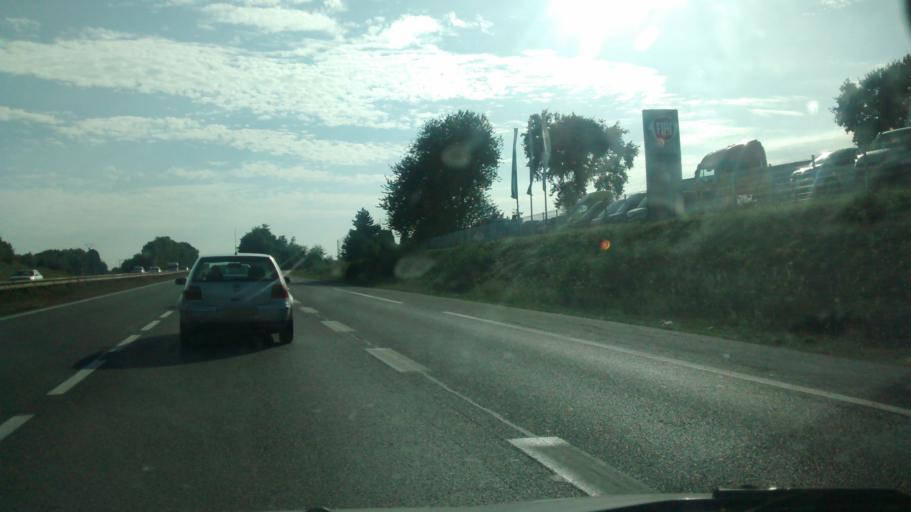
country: FR
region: Brittany
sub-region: Departement d'Ille-et-Vilaine
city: Chantepie
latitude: 48.0942
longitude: -1.6232
